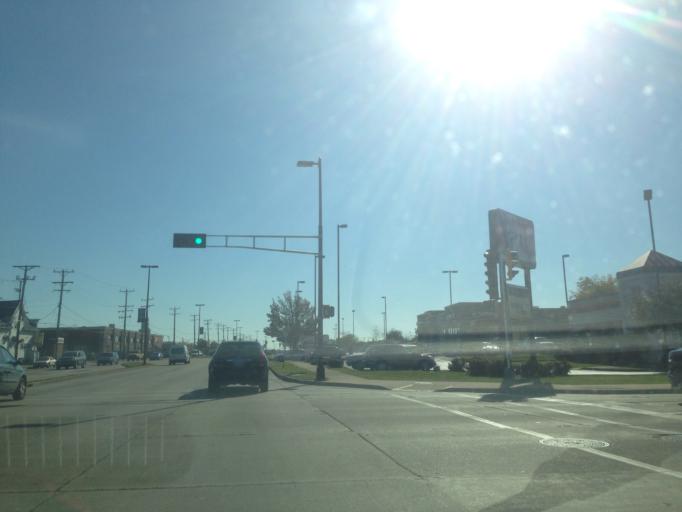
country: US
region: Wisconsin
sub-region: Milwaukee County
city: West Milwaukee
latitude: 43.0171
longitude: -87.9679
